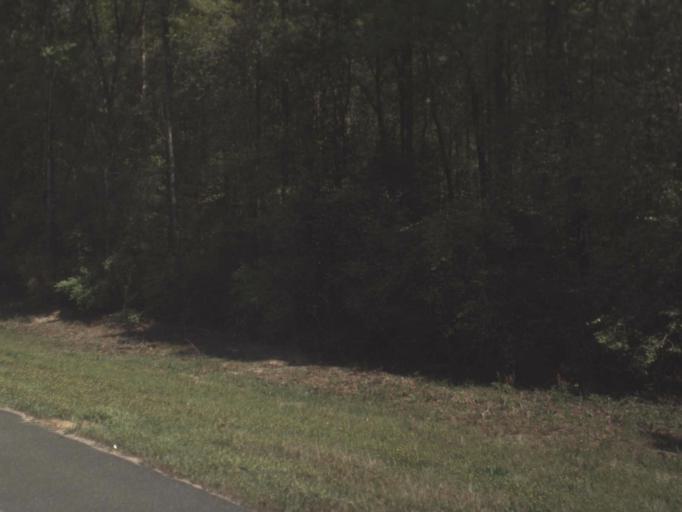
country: US
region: Florida
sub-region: Okaloosa County
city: Crestview
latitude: 30.7063
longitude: -86.7728
